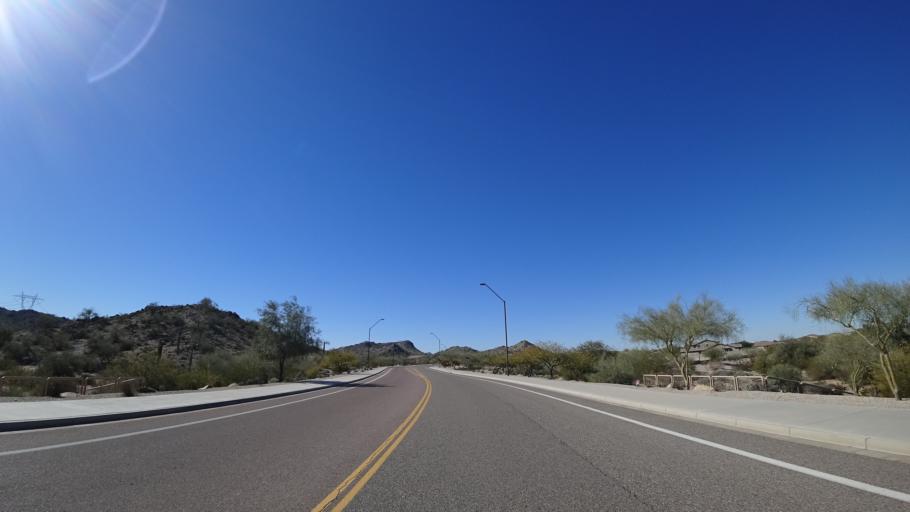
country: US
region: Arizona
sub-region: Maricopa County
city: Goodyear
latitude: 33.3239
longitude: -112.4404
